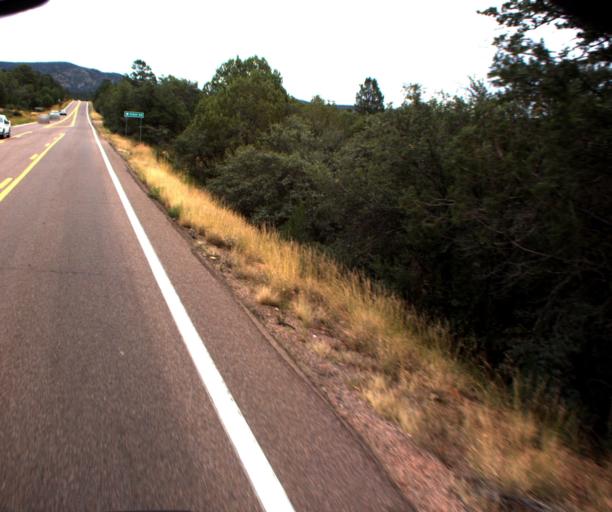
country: US
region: Arizona
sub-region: Gila County
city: Star Valley
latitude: 34.2637
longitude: -111.2206
